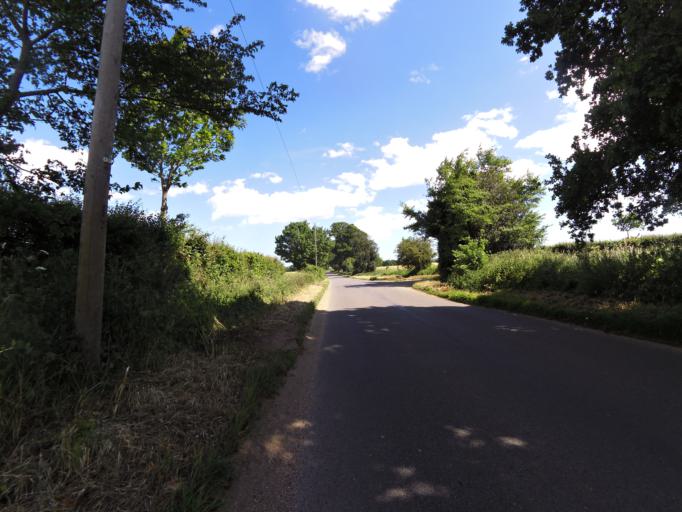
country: GB
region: England
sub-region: Suffolk
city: Kesgrave
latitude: 52.0229
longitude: 1.2119
